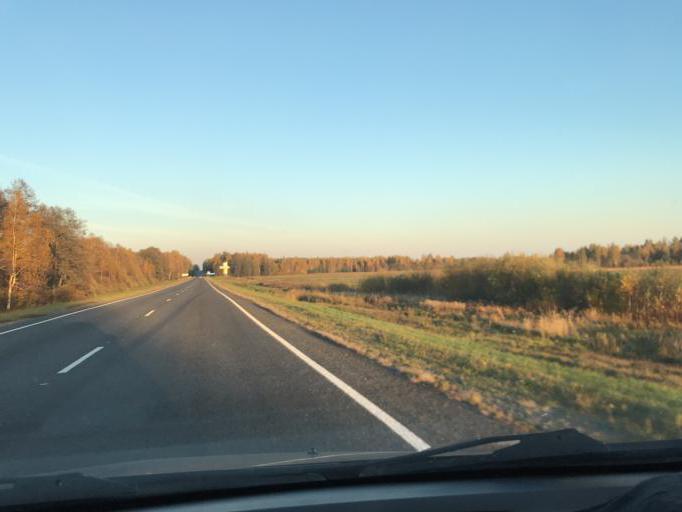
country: BY
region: Mogilev
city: Hlusk
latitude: 53.0644
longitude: 28.5279
